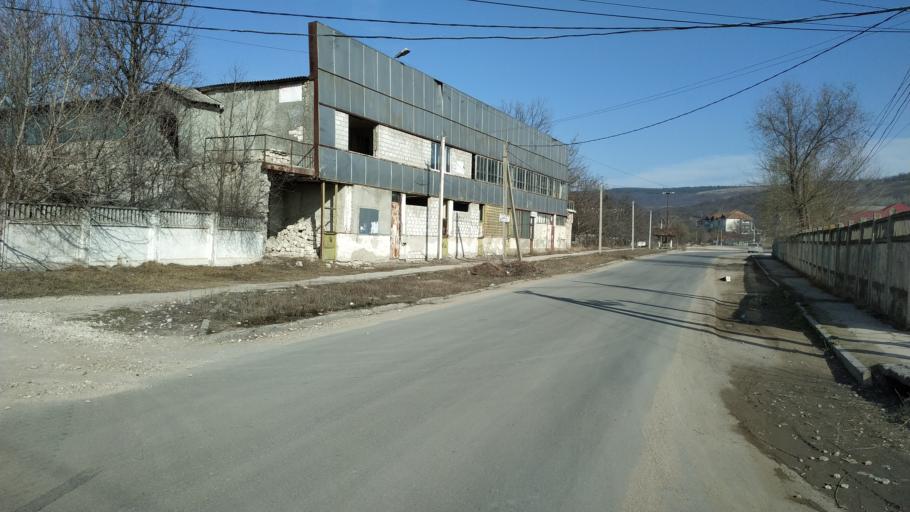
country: MD
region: Nisporeni
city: Nisporeni
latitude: 47.0726
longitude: 28.1759
